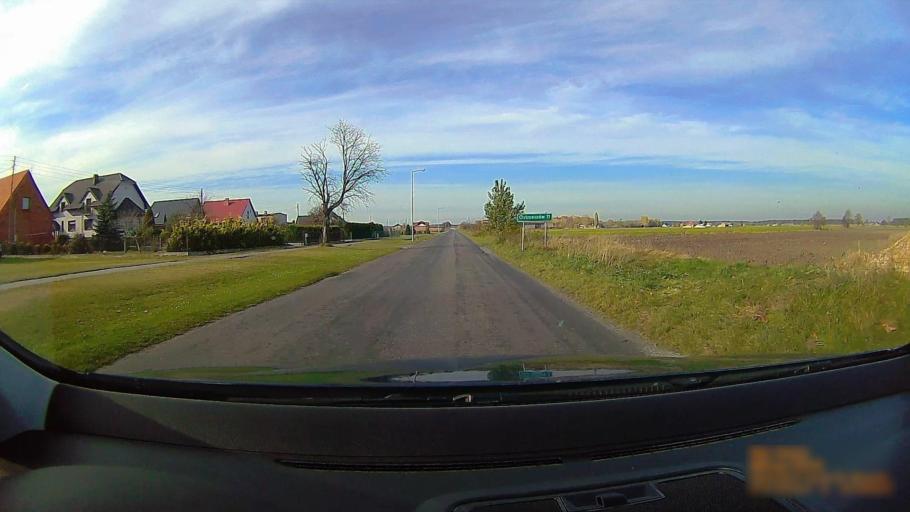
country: PL
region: Greater Poland Voivodeship
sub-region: Powiat ostrzeszowski
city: Doruchow
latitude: 51.4214
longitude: 18.0637
